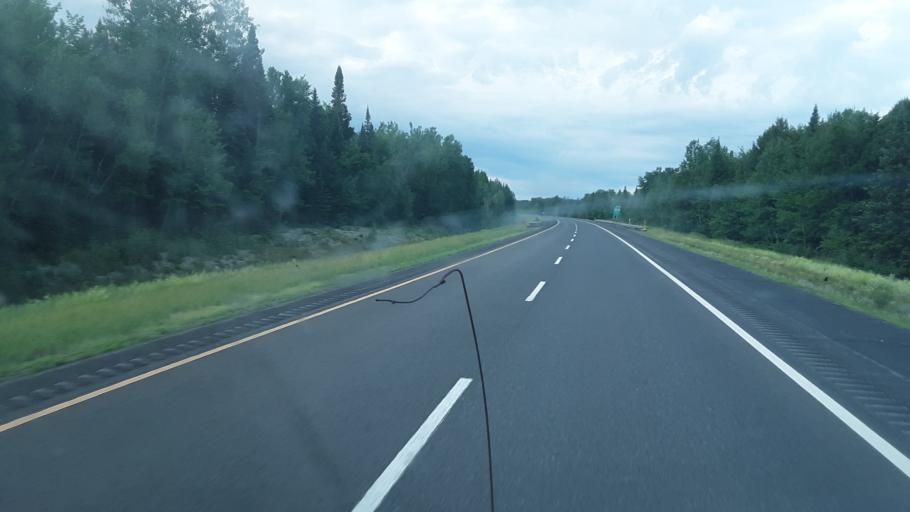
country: US
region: Maine
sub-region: Penobscot County
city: Patten
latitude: 45.8930
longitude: -68.4016
